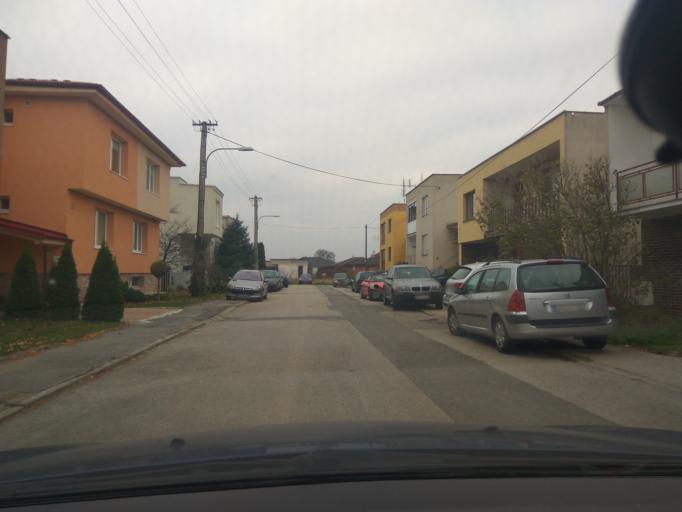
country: SK
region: Trnavsky
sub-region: Okres Trnava
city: Piestany
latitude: 48.6081
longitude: 17.8640
